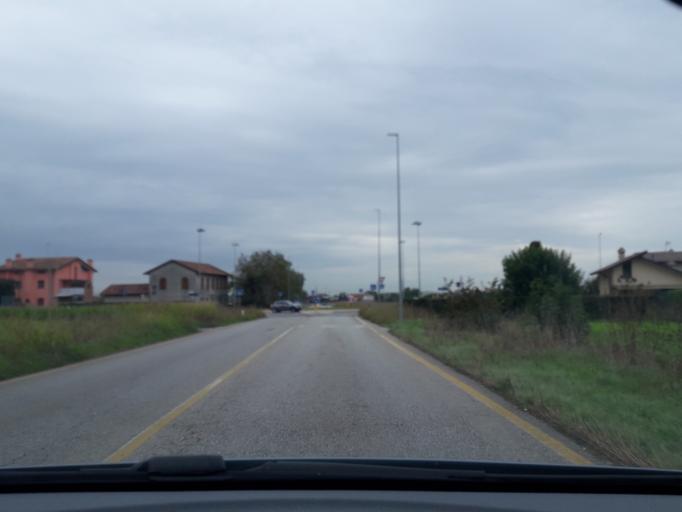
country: IT
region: Friuli Venezia Giulia
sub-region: Provincia di Udine
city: Povoletto
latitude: 46.1041
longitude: 13.2602
